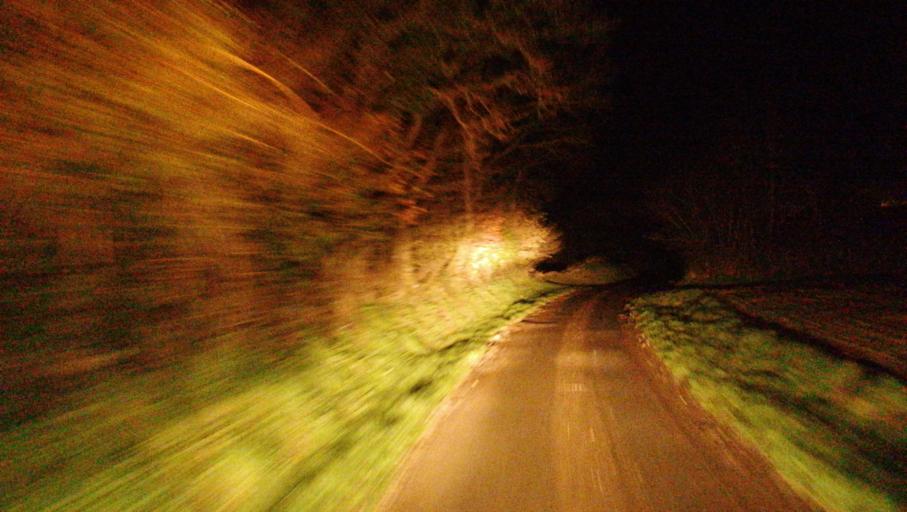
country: FR
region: Brittany
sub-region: Departement des Cotes-d'Armor
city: Plehedel
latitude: 48.6765
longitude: -3.0307
